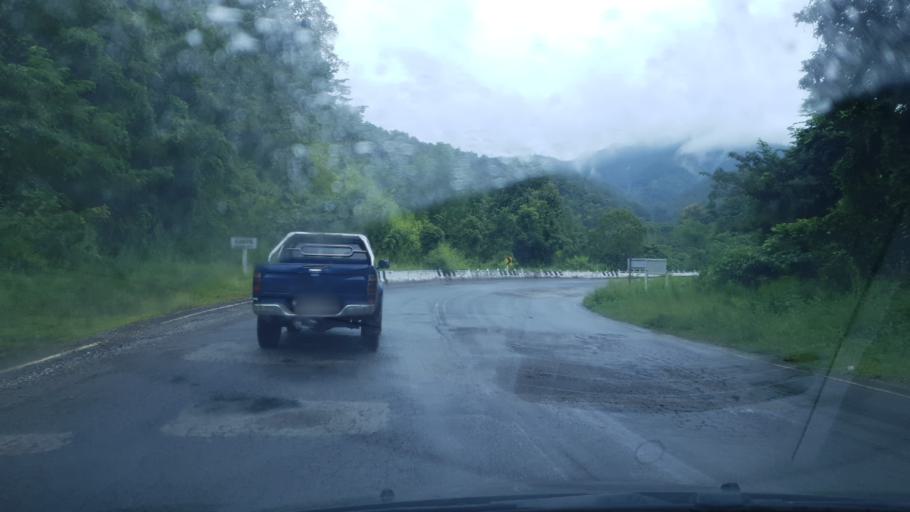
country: TH
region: Mae Hong Son
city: Mae La Noi
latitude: 18.2924
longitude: 97.9311
